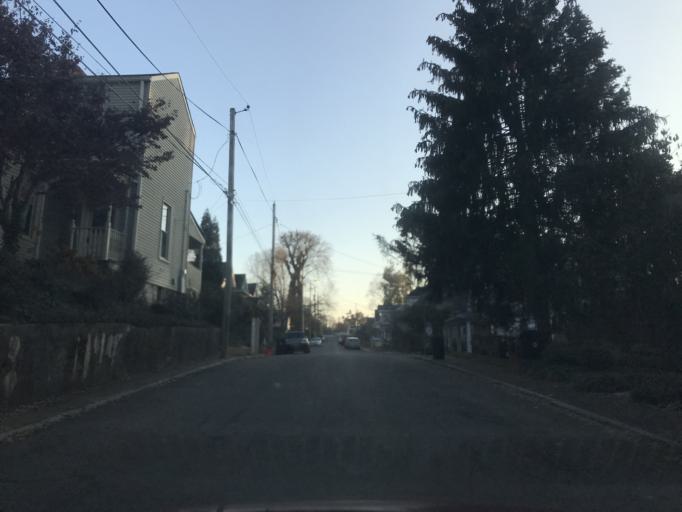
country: US
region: Indiana
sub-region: Clark County
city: Jeffersonville
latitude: 38.2553
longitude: -85.7035
